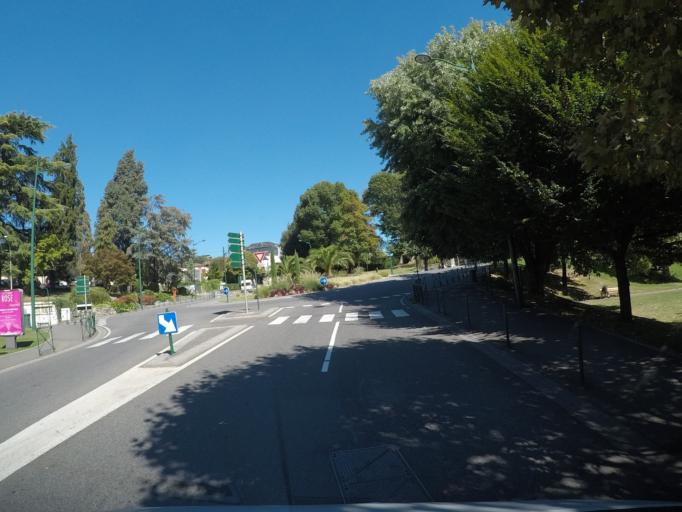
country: FR
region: Midi-Pyrenees
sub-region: Departement des Hautes-Pyrenees
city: Lourdes
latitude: 43.0990
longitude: -0.0454
